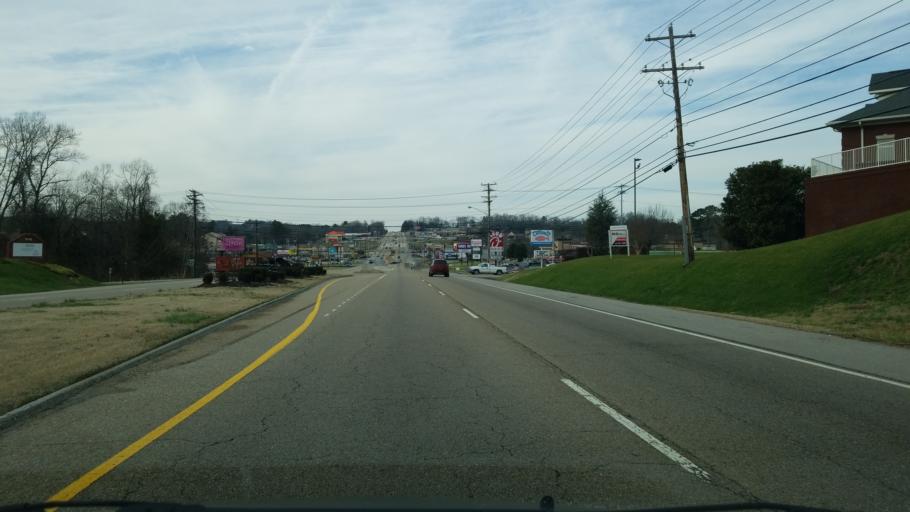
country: US
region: Tennessee
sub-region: Loudon County
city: Lenoir City
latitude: 35.8244
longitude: -84.2729
